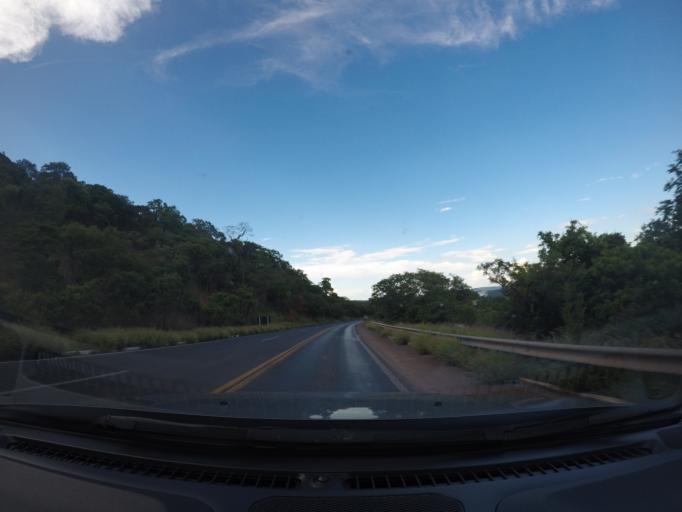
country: BR
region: Bahia
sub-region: Ibotirama
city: Ibotirama
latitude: -12.1354
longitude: -43.3511
